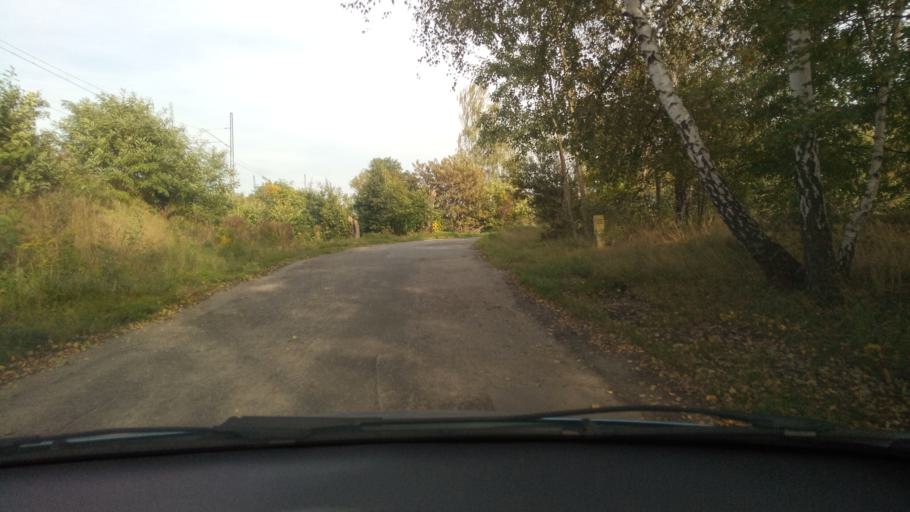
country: PL
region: Silesian Voivodeship
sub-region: Sosnowiec
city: Sosnowiec
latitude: 50.2617
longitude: 19.1333
